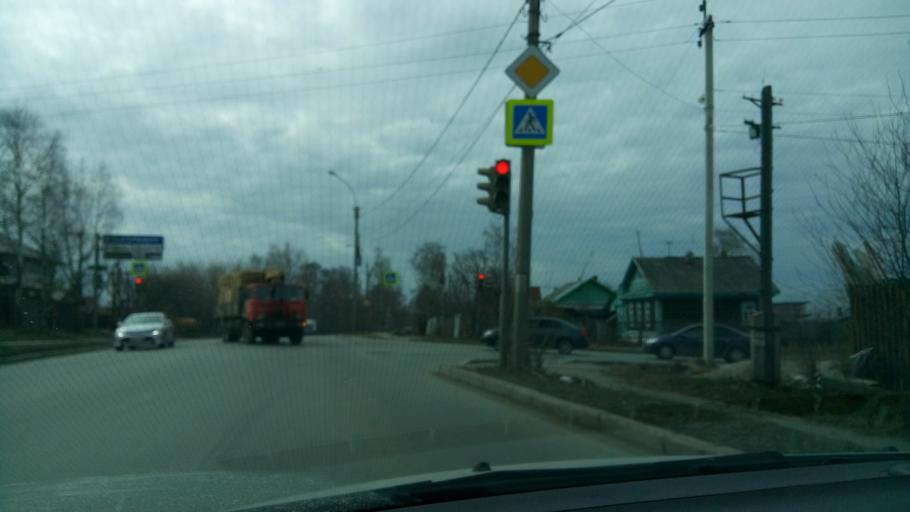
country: RU
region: Sverdlovsk
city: Beryozovsky
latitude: 56.8852
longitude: 60.7231
